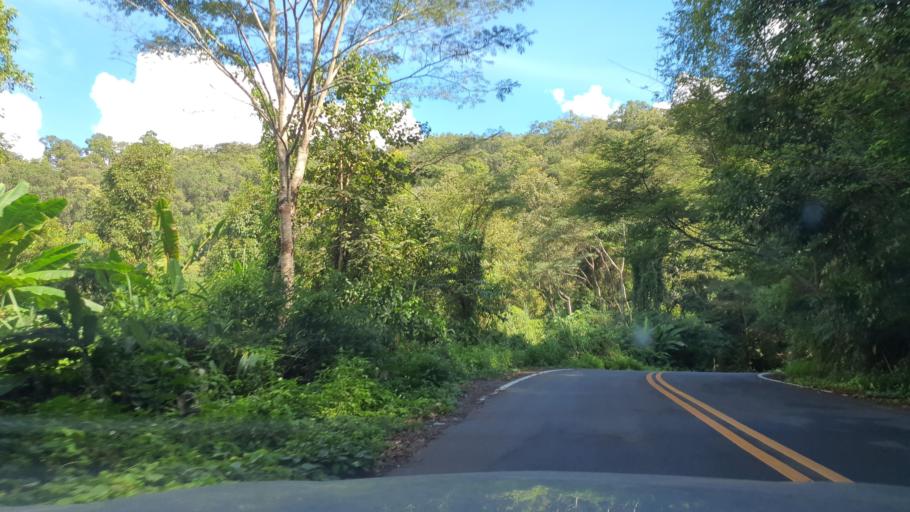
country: TH
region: Chiang Rai
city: Wiang Pa Pao
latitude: 19.3078
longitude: 99.3594
